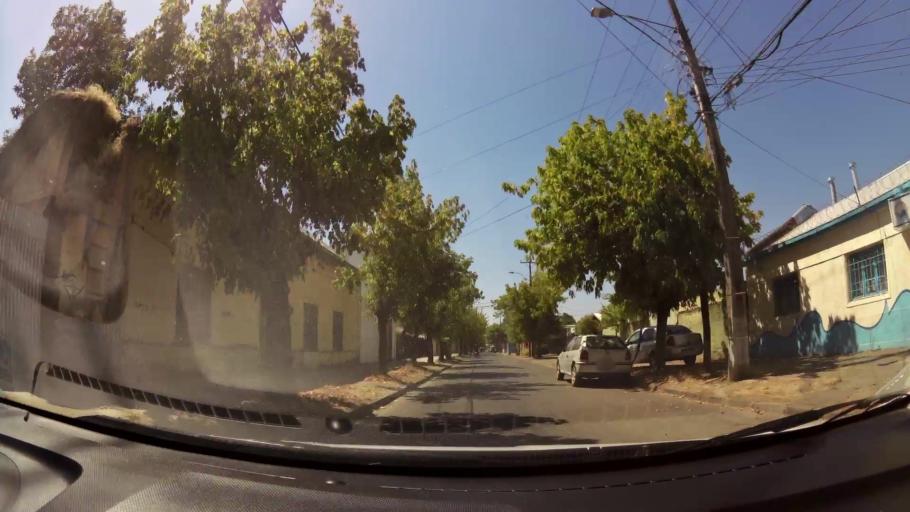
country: CL
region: Maule
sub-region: Provincia de Talca
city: Talca
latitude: -35.4154
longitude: -71.6601
